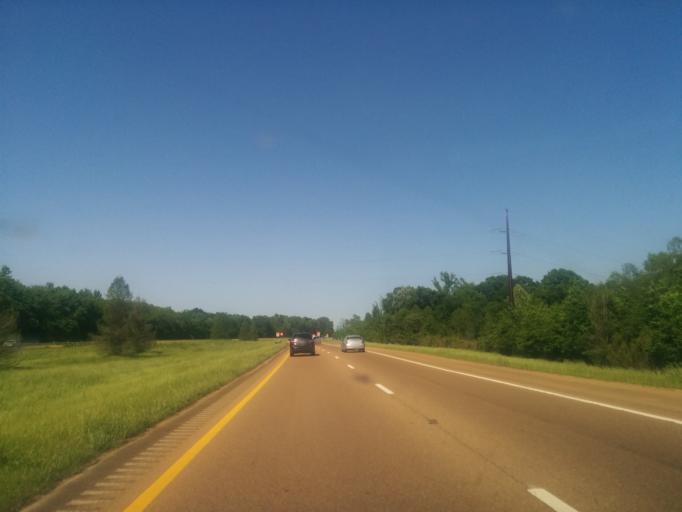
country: US
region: Mississippi
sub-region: Madison County
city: Madison
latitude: 32.5015
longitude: -90.1192
